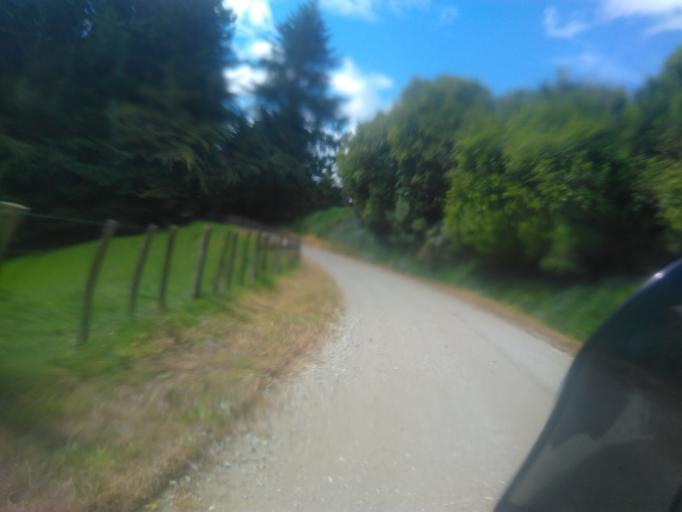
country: NZ
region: Hawke's Bay
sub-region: Wairoa District
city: Wairoa
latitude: -38.7743
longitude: 177.6373
